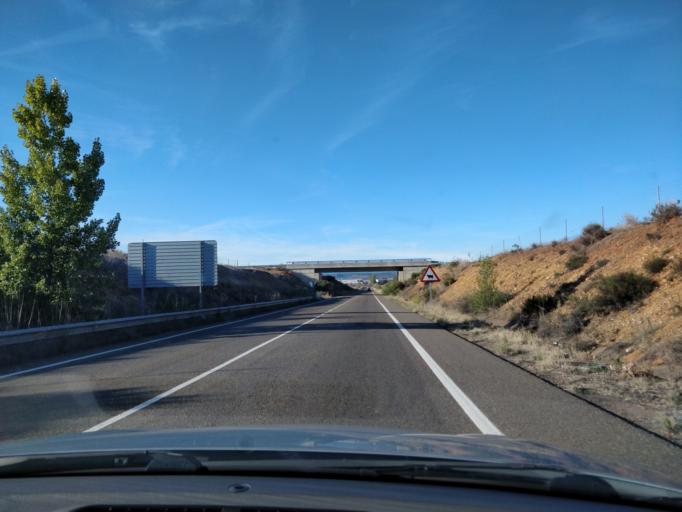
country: ES
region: Castille and Leon
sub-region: Provincia de Leon
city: San Andres del Rabanedo
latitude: 42.5776
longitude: -5.6203
